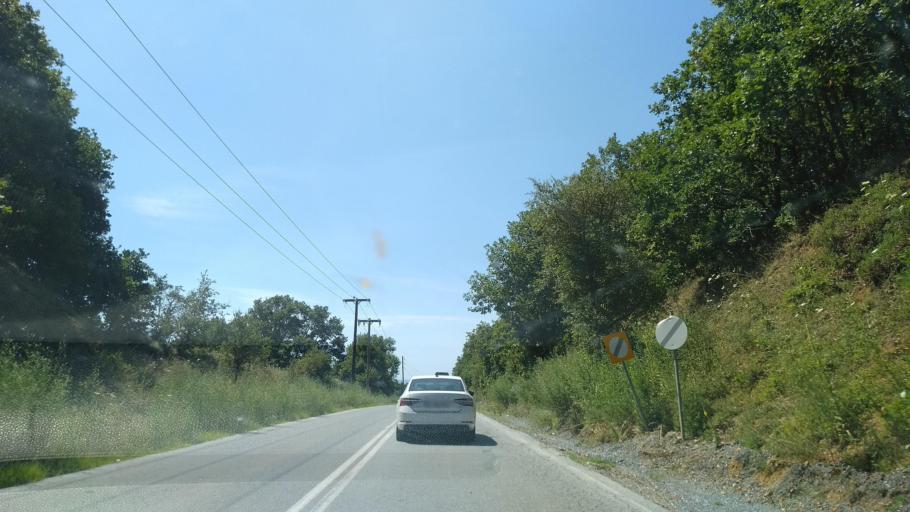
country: GR
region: Central Macedonia
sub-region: Nomos Chalkidikis
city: Megali Panagia
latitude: 40.4555
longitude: 23.6578
